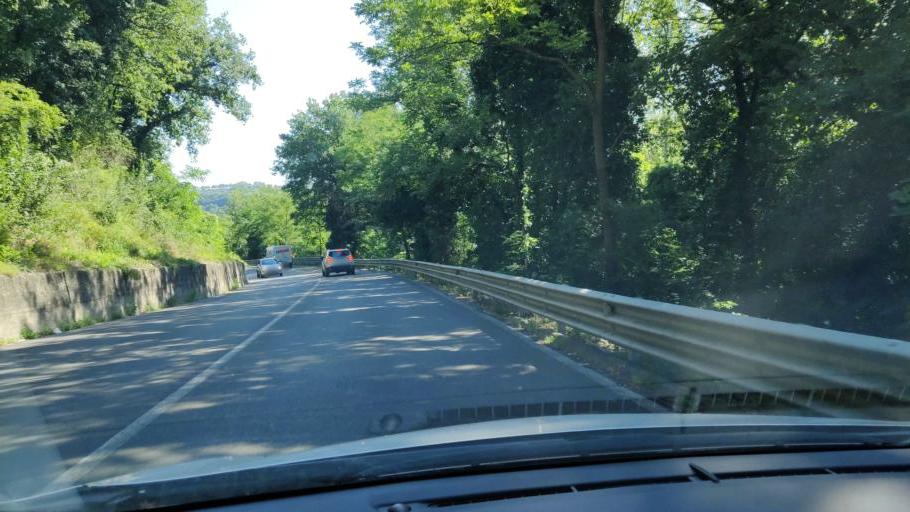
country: IT
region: Umbria
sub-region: Provincia di Perugia
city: Todi
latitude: 42.7856
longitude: 12.4161
